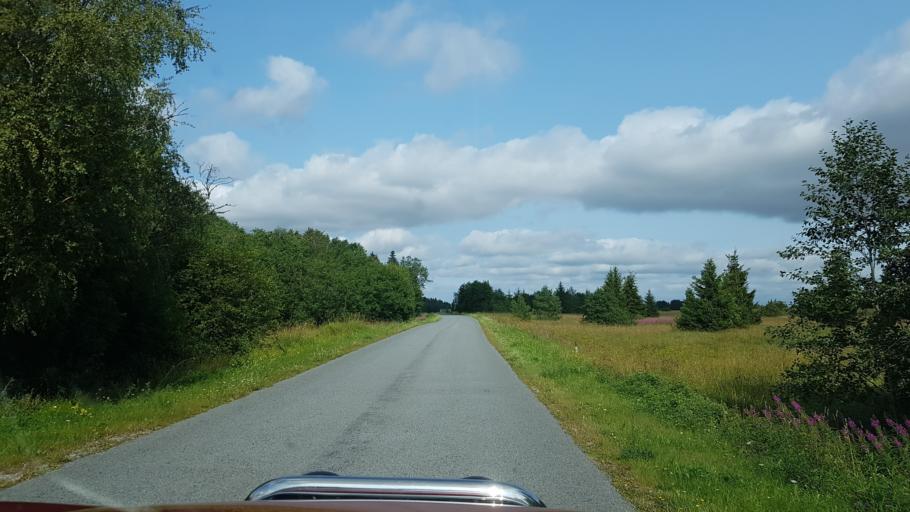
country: EE
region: Laeaene-Virumaa
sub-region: Tapa vald
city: Tapa
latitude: 59.3286
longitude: 26.0329
